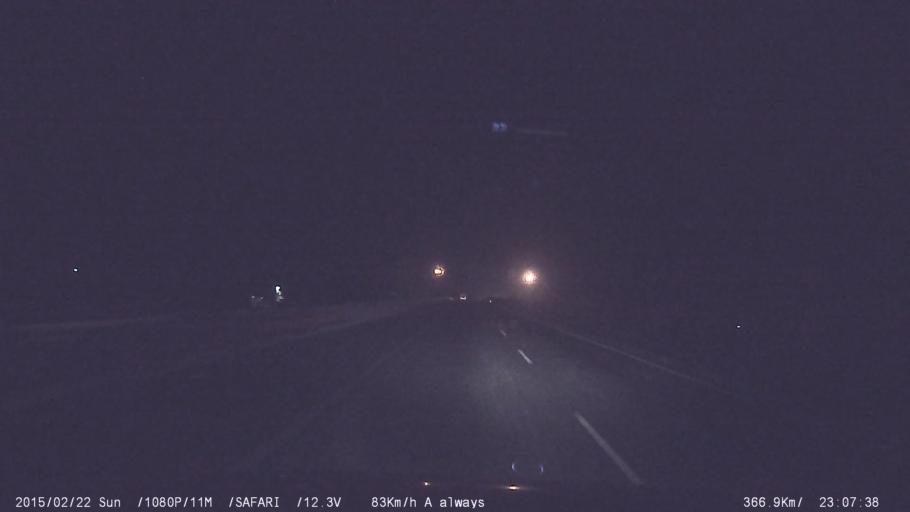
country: IN
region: Tamil Nadu
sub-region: Namakkal
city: Rasipuram
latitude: 11.4423
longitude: 78.1582
